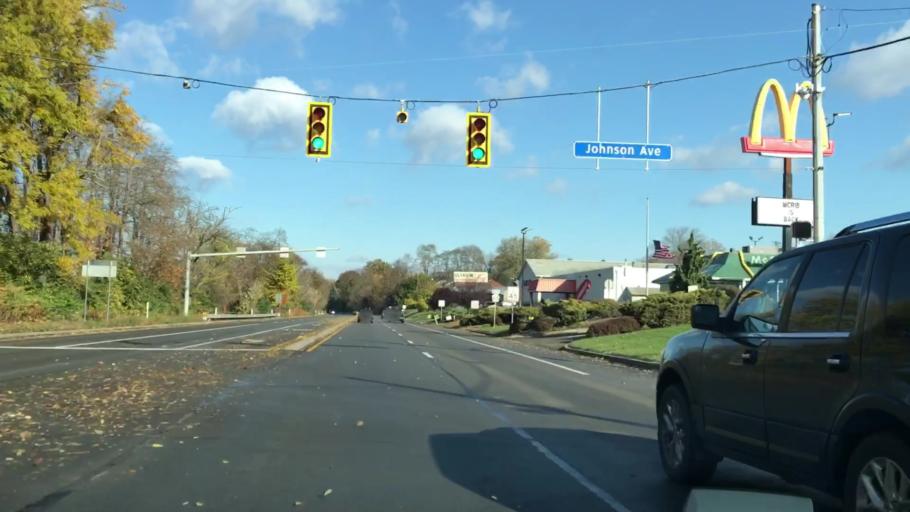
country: US
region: Pennsylvania
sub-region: Beaver County
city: Baden
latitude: 40.6328
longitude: -80.2302
